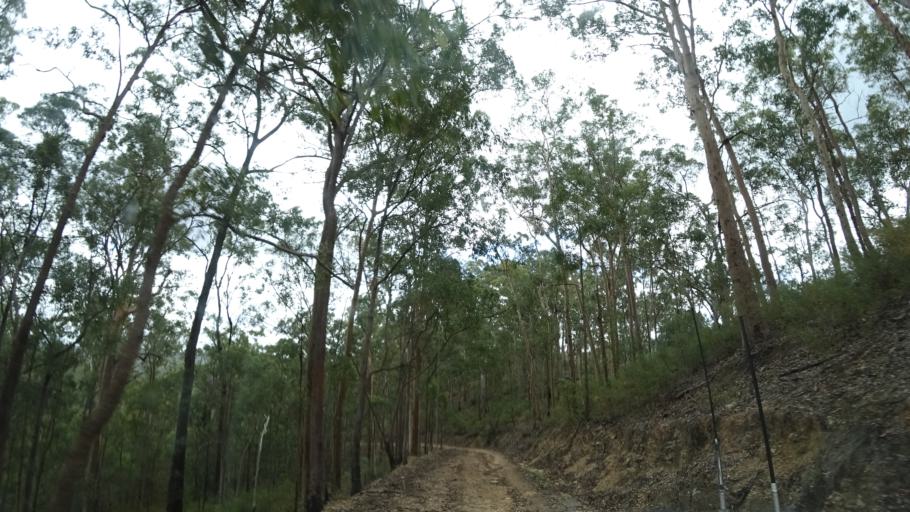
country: AU
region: Queensland
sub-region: Moreton Bay
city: Highvale
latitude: -27.4267
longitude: 152.7687
